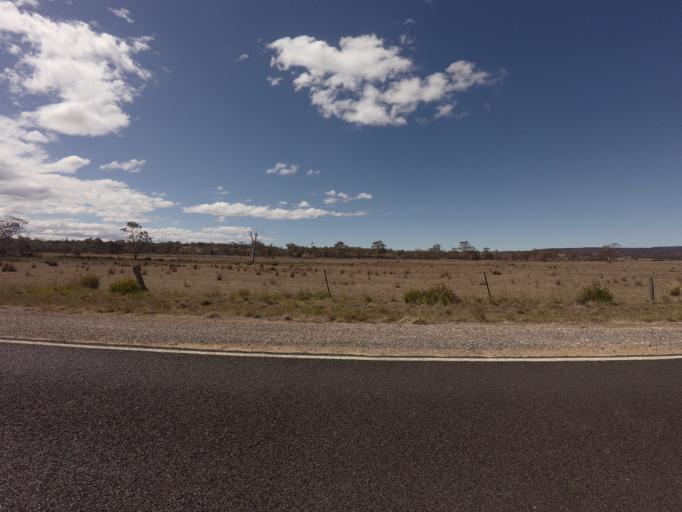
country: AU
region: Tasmania
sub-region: Break O'Day
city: St Helens
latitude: -42.0426
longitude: 148.0342
